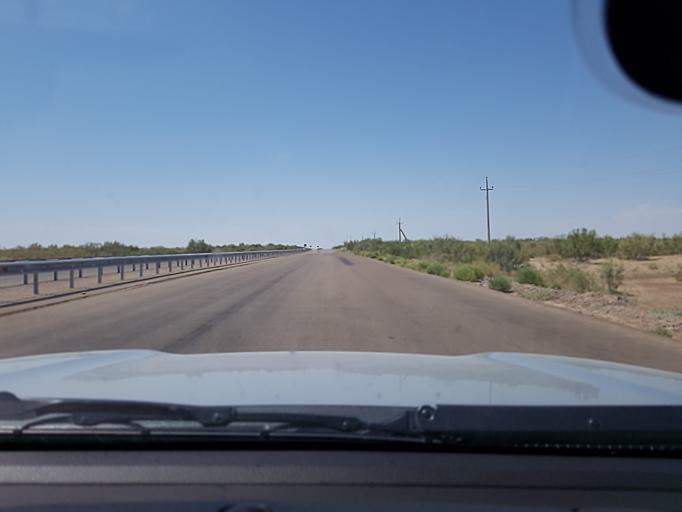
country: TM
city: Akdepe
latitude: 41.7367
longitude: 59.0230
